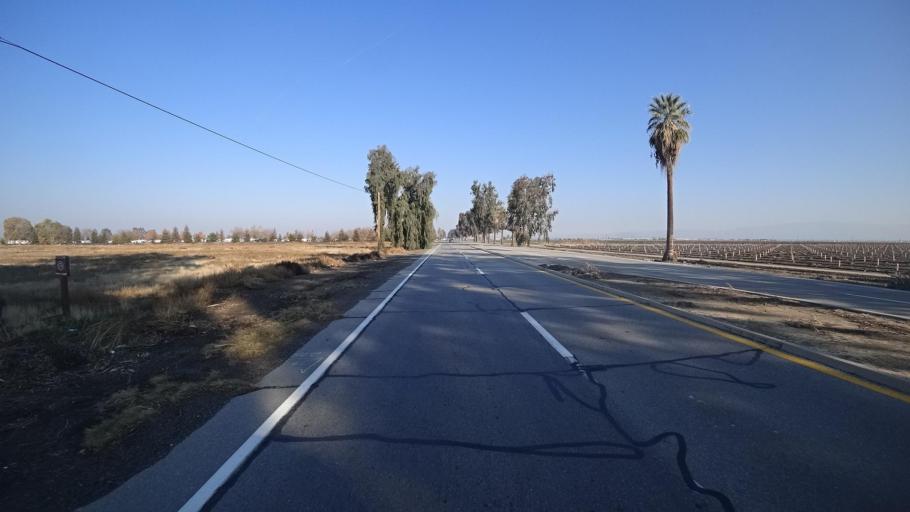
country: US
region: California
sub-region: Kern County
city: Greenfield
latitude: 35.2027
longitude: -119.0033
